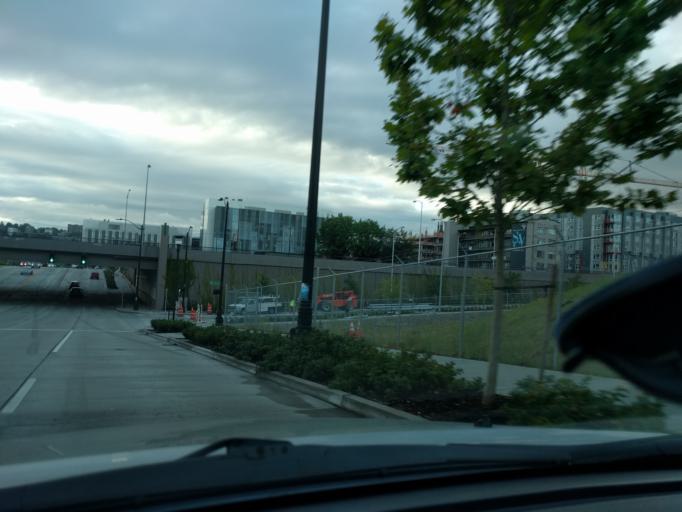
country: US
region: Washington
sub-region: King County
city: Seattle
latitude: 47.6243
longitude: -122.3450
